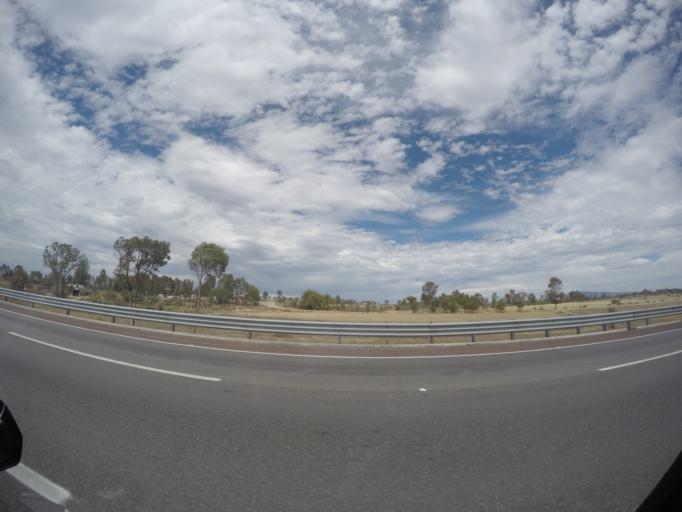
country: MX
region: Queretaro
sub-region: San Juan del Rio
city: El Cazadero
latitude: 20.2566
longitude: -99.8483
